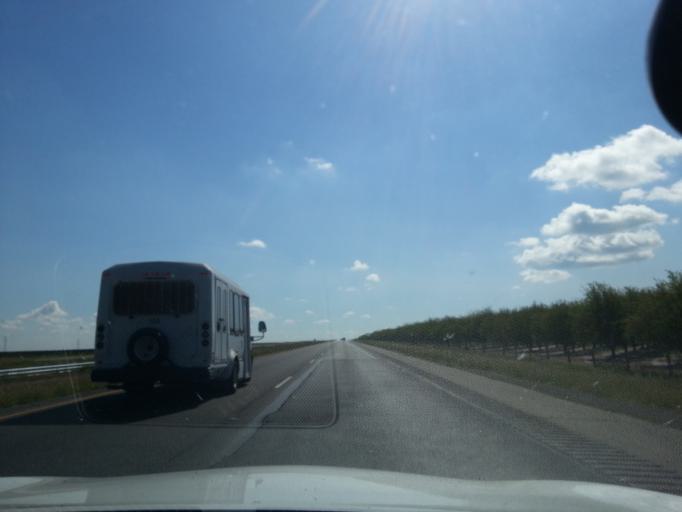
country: US
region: California
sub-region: Fresno County
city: Coalinga
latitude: 36.3851
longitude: -120.3491
